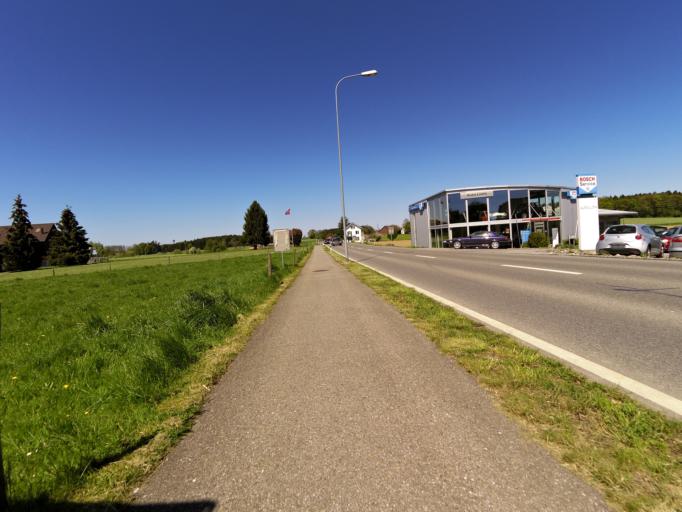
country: CH
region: Thurgau
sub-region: Weinfelden District
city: Berg
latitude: 47.5837
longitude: 9.1687
